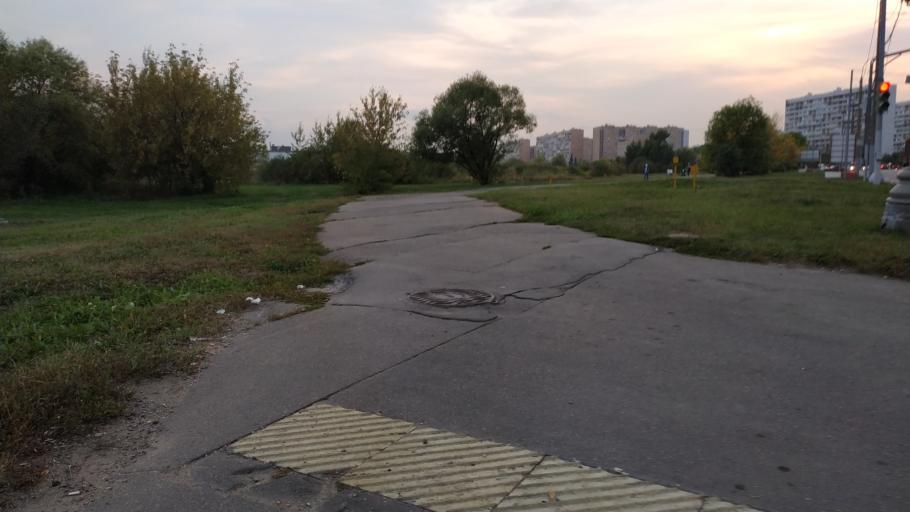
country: RU
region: Moscow
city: Solntsevo
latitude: 55.6398
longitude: 37.3730
